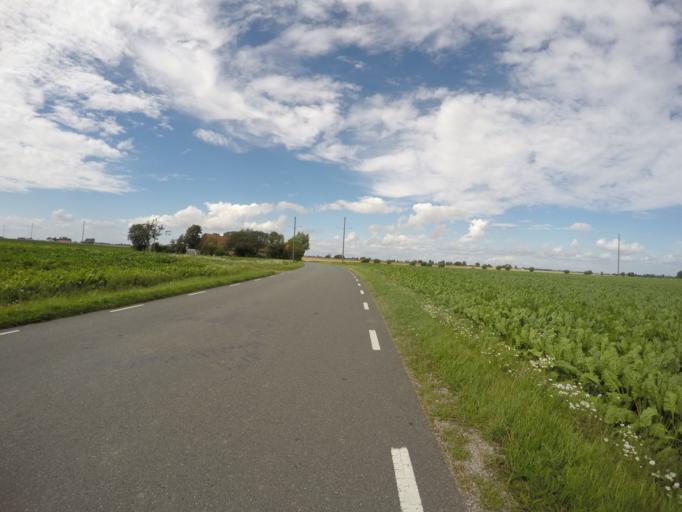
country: SE
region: Skane
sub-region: Ystads Kommun
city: Kopingebro
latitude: 55.4167
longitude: 14.1501
